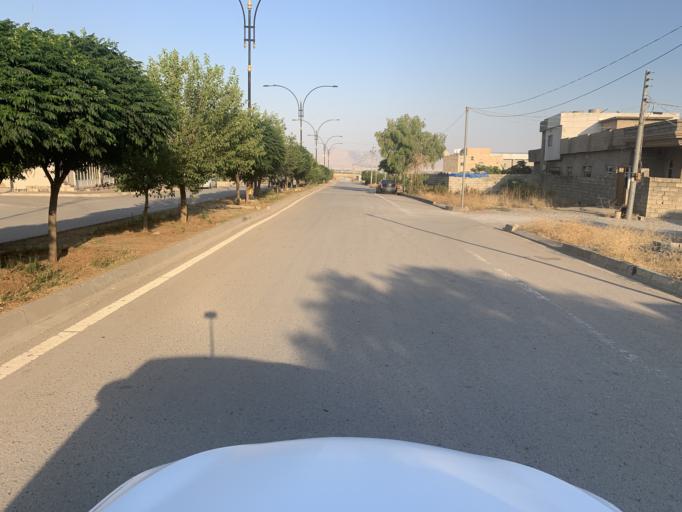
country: IQ
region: As Sulaymaniyah
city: Raniye
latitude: 36.2384
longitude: 44.8794
